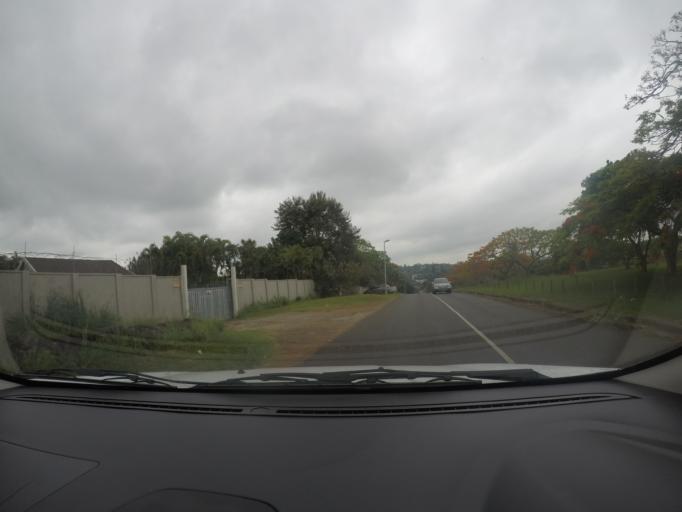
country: ZA
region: KwaZulu-Natal
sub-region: uThungulu District Municipality
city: Empangeni
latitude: -28.7628
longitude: 31.8917
